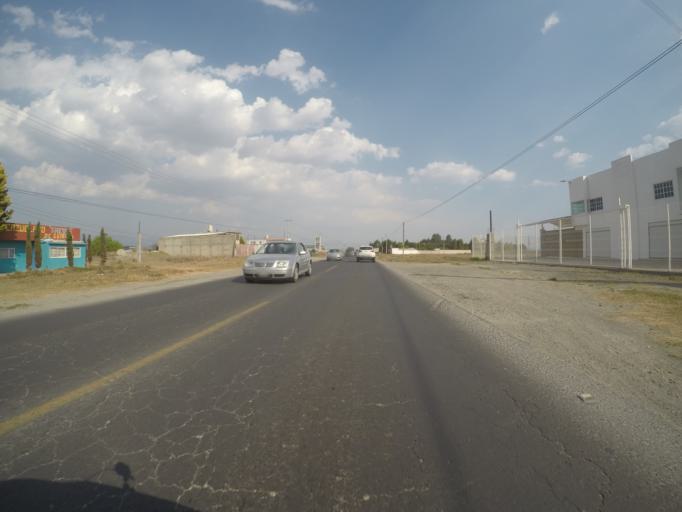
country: MX
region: Morelos
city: Chapultepec
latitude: 19.1945
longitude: -99.5397
